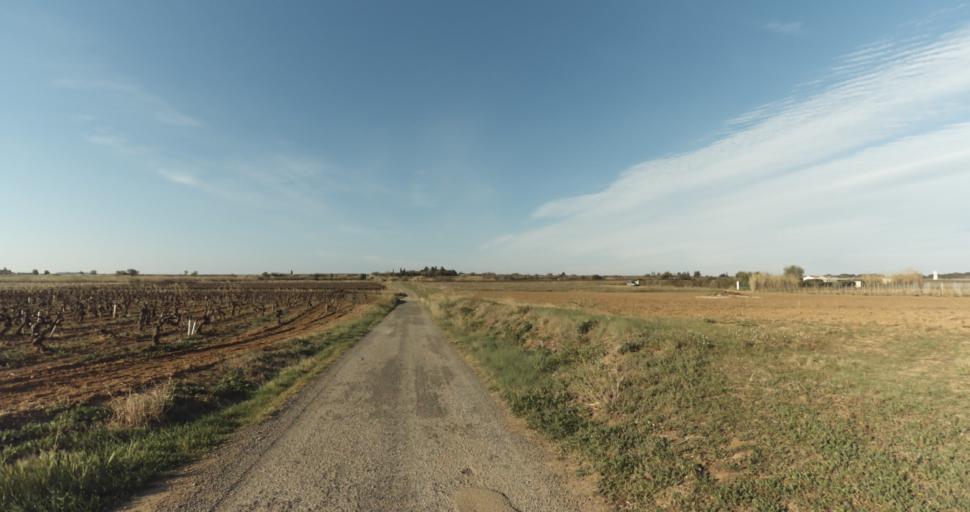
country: FR
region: Languedoc-Roussillon
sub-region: Departement de l'Herault
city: Marseillan
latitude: 43.3674
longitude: 3.5154
